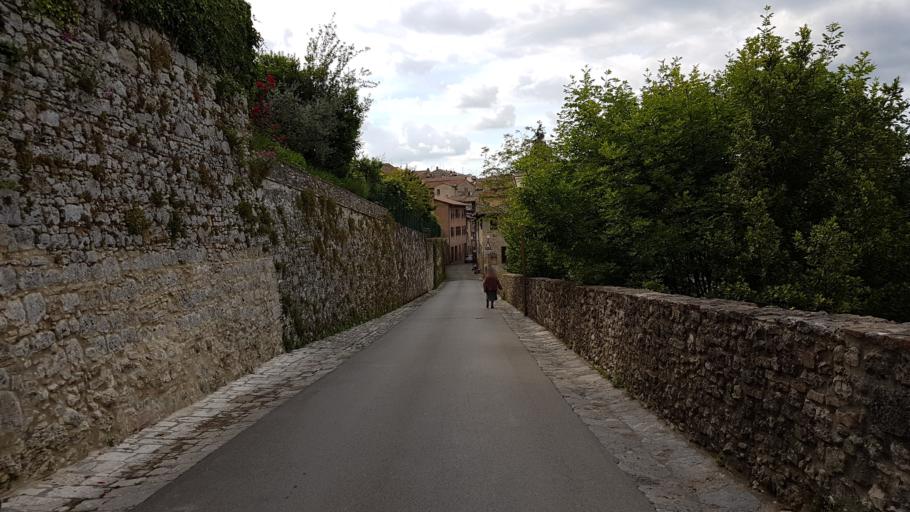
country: IT
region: Tuscany
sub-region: Provincia di Siena
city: San Gimignano
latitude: 43.4685
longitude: 11.0443
